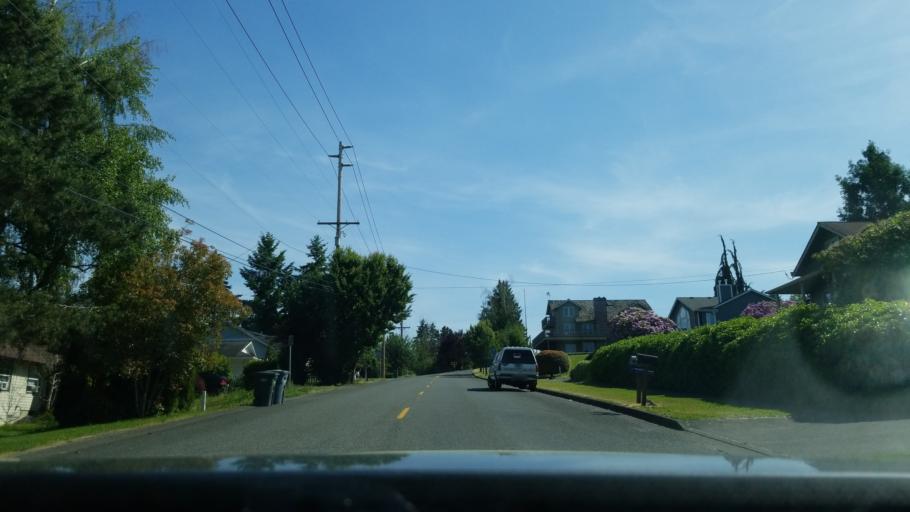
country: US
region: Washington
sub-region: Pierce County
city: Puyallup
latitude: 47.1785
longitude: -122.3054
